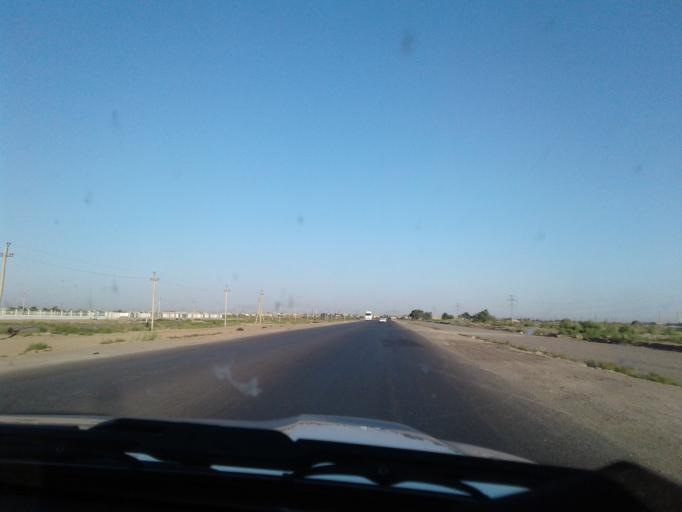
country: TM
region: Mary
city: Mary
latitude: 37.5737
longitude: 61.8026
